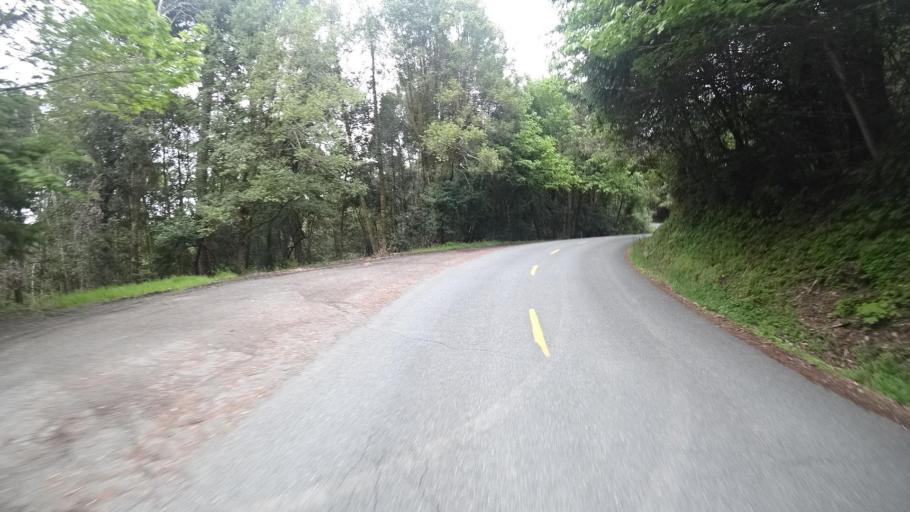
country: US
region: California
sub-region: Humboldt County
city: Blue Lake
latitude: 40.9494
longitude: -123.8400
